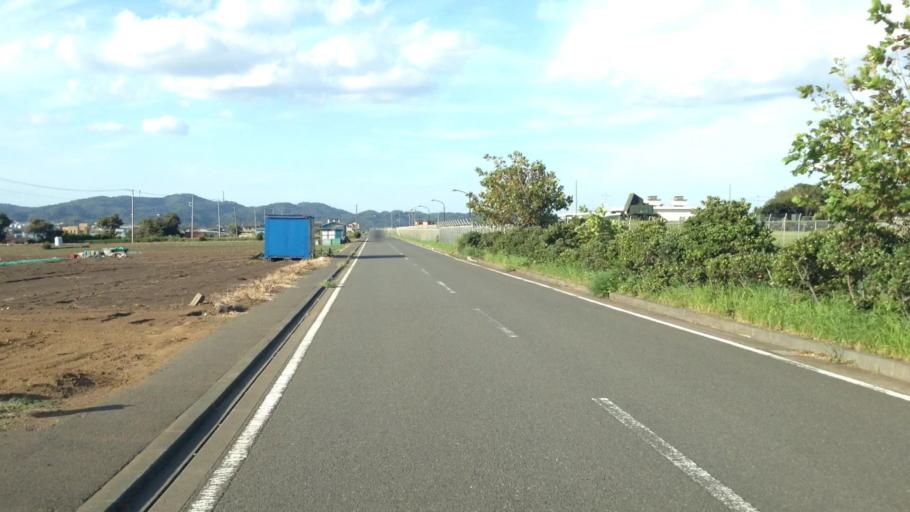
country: JP
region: Kanagawa
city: Miura
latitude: 35.1988
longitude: 139.6132
